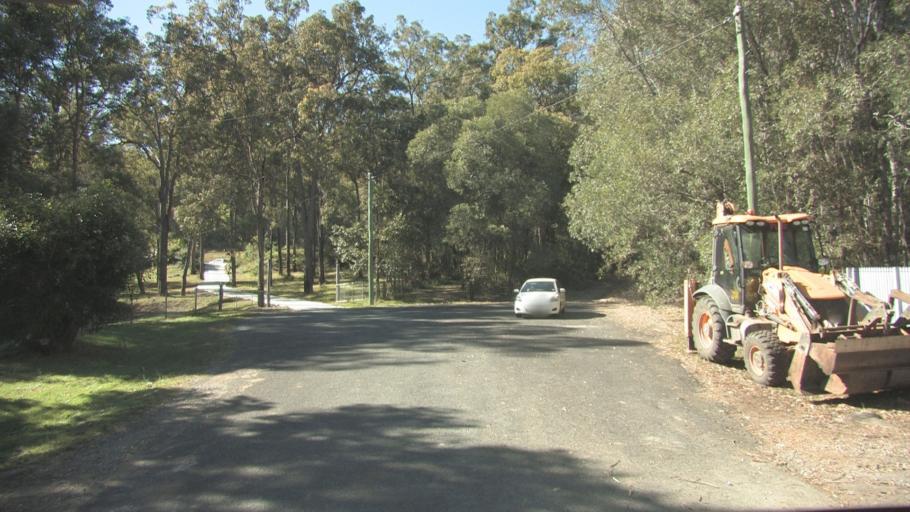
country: AU
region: Queensland
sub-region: Logan
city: Windaroo
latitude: -27.7658
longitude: 153.1452
